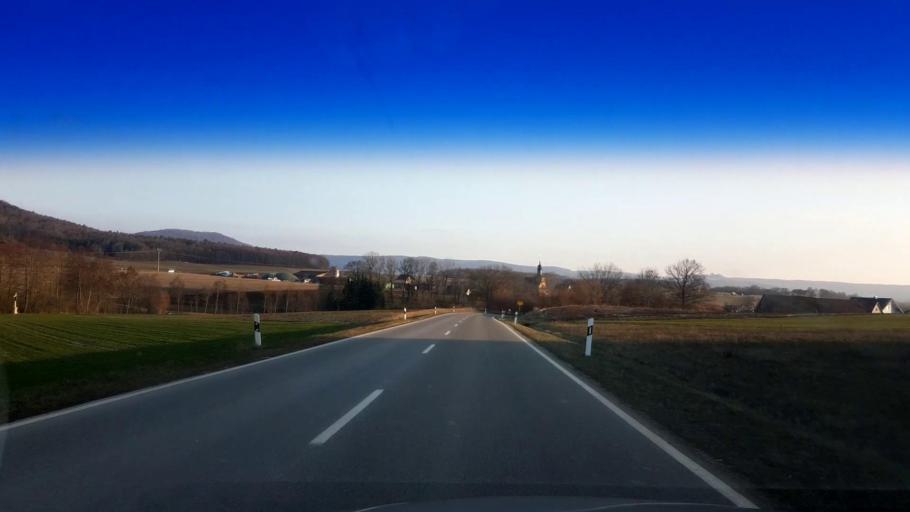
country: DE
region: Bavaria
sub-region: Upper Franconia
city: Schesslitz
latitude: 50.0074
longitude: 11.0143
